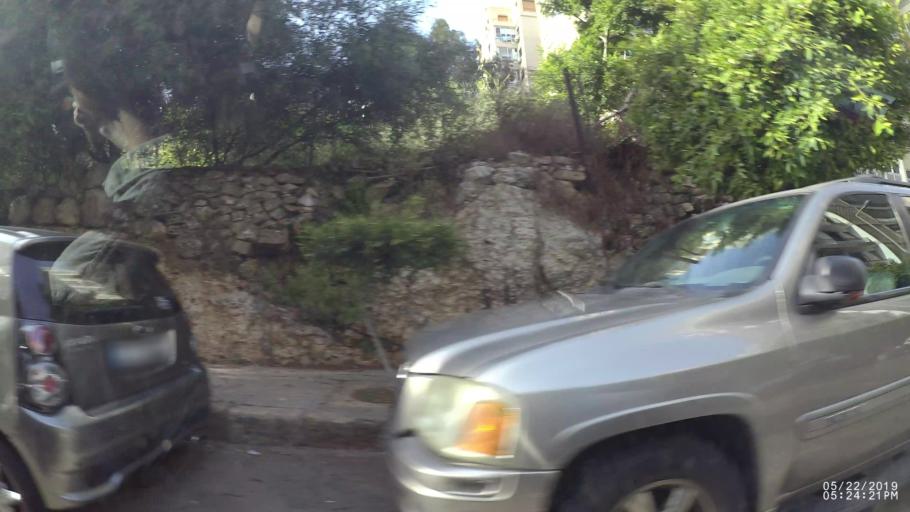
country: LB
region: Beyrouth
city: Ra's Bayrut
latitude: 33.8891
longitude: 35.4777
